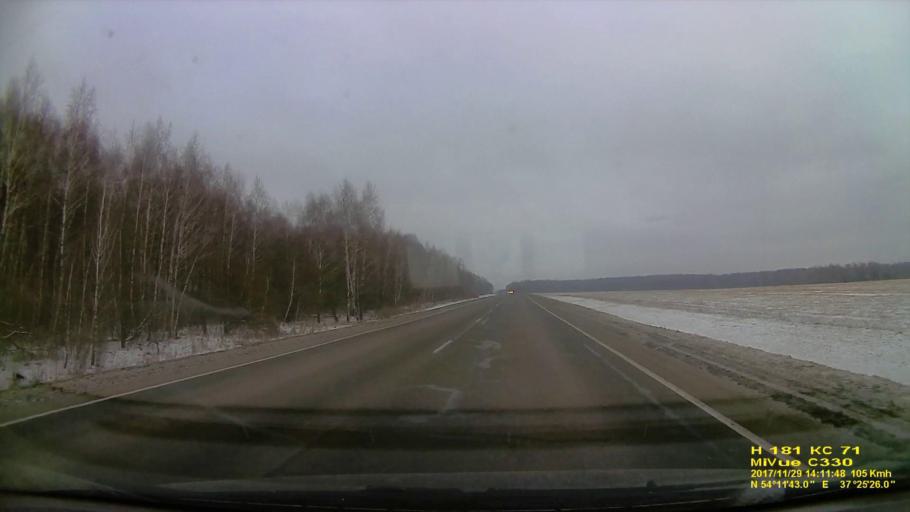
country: RU
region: Tula
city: Barsuki
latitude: 54.1950
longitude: 37.4242
